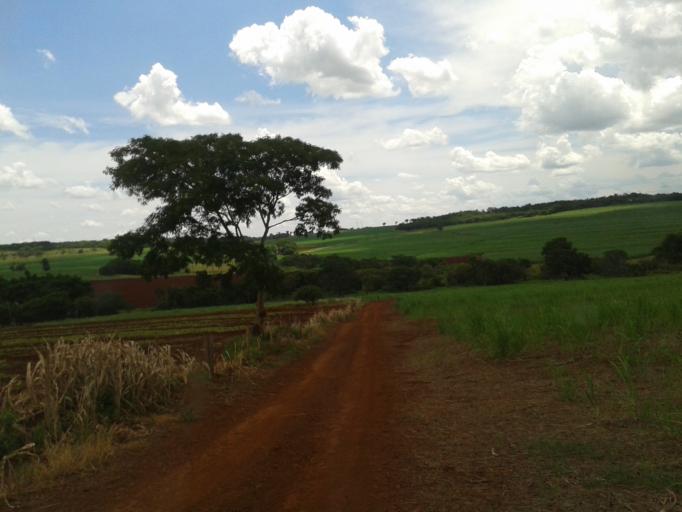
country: BR
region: Minas Gerais
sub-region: Centralina
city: Centralina
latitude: -18.6813
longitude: -49.2326
